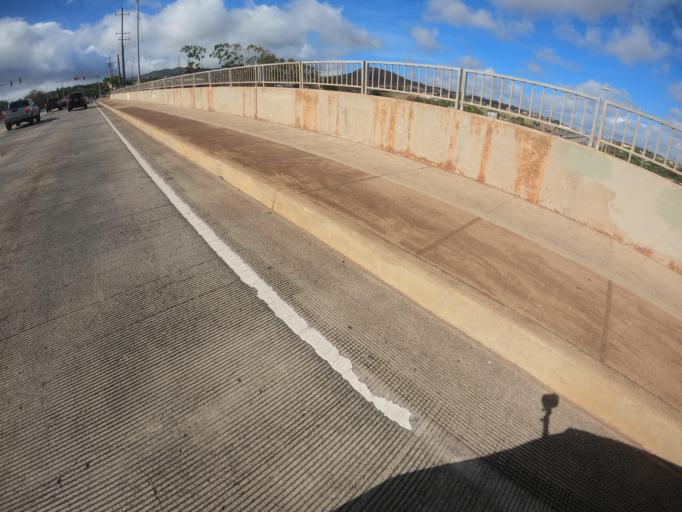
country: US
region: Hawaii
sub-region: Honolulu County
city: Makakilo City
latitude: 21.3420
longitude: -158.0776
